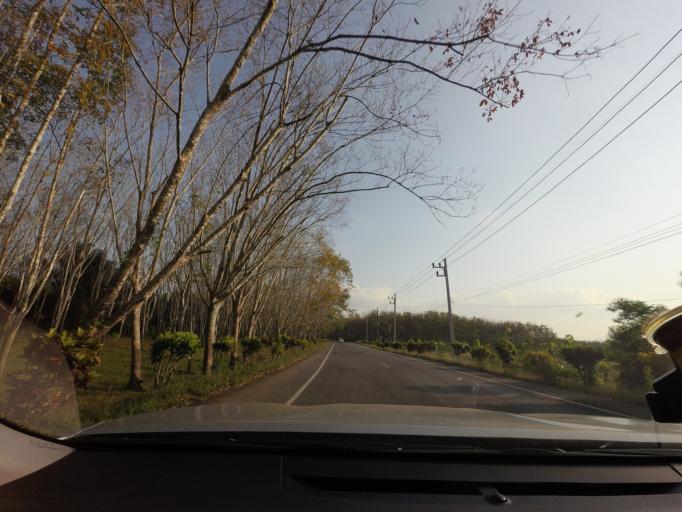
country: TH
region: Surat Thani
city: Phrasaeng
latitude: 8.5712
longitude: 99.2827
